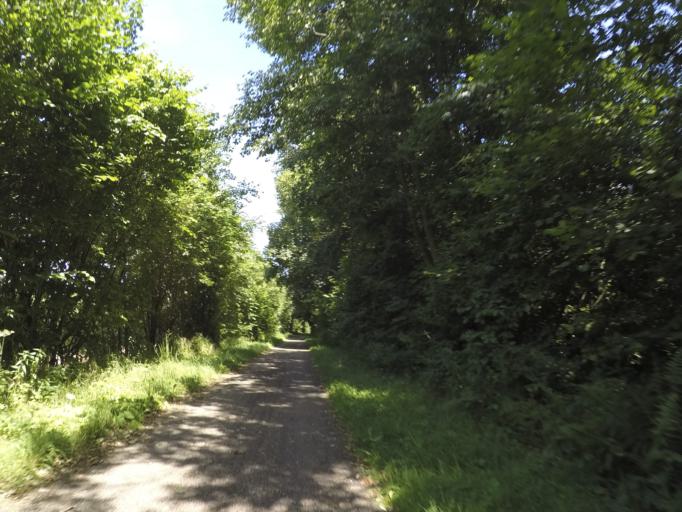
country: BE
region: Wallonia
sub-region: Province de Namur
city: Havelange
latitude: 50.3908
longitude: 5.2656
